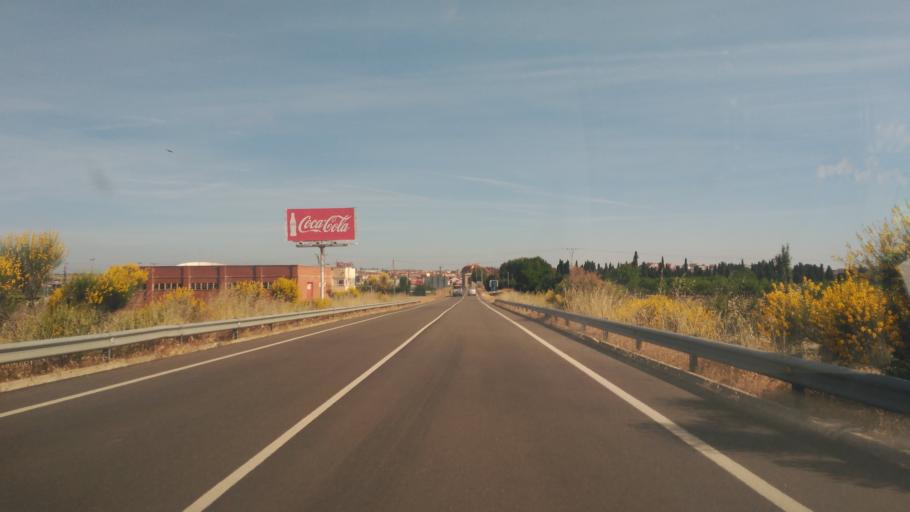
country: ES
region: Castille and Leon
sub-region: Provincia de Zamora
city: Zamora
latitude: 41.4846
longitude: -5.7428
